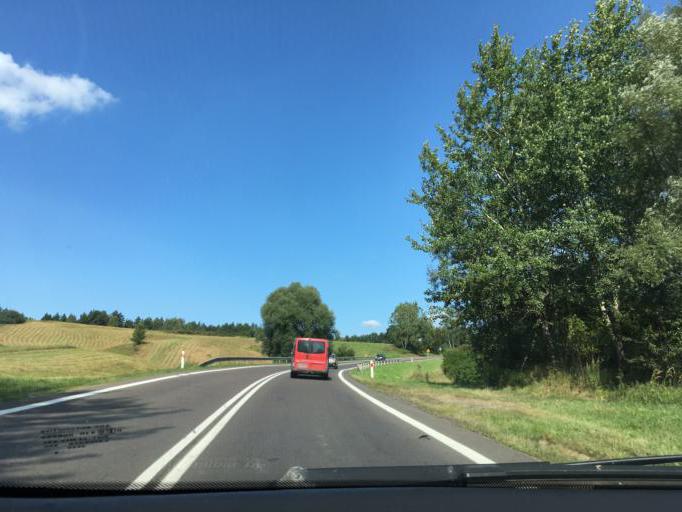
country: PL
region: Subcarpathian Voivodeship
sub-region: Powiat sanocki
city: Zagorz
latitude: 49.4987
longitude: 22.3031
